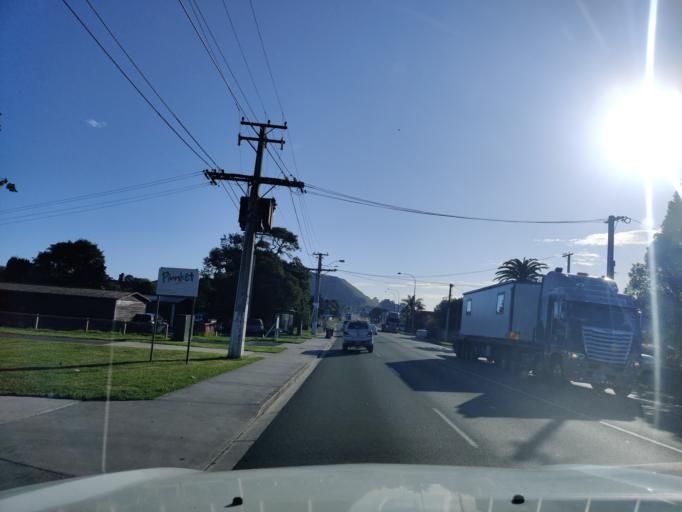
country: NZ
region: Auckland
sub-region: Auckland
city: Tamaki
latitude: -36.9054
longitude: 174.8406
